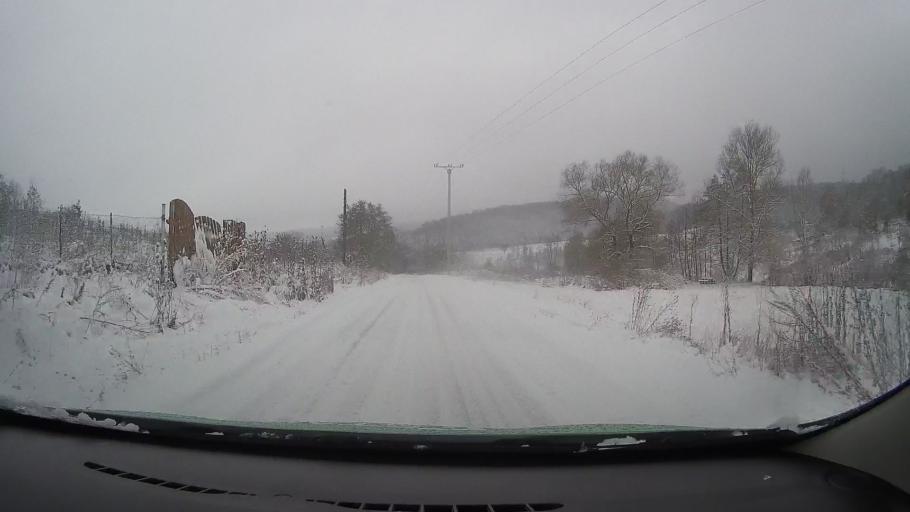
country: RO
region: Hunedoara
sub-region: Comuna Carjiti
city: Carjiti
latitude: 45.8335
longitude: 22.8407
